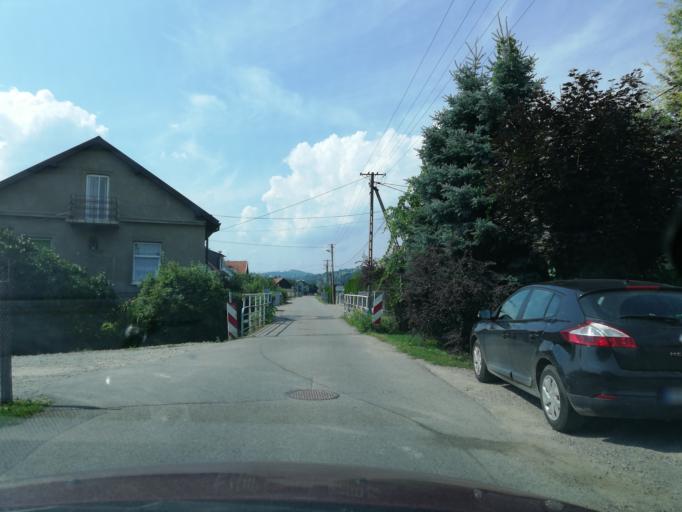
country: PL
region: Lesser Poland Voivodeship
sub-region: Powiat nowosadecki
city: Chelmiec
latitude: 49.6274
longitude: 20.6714
